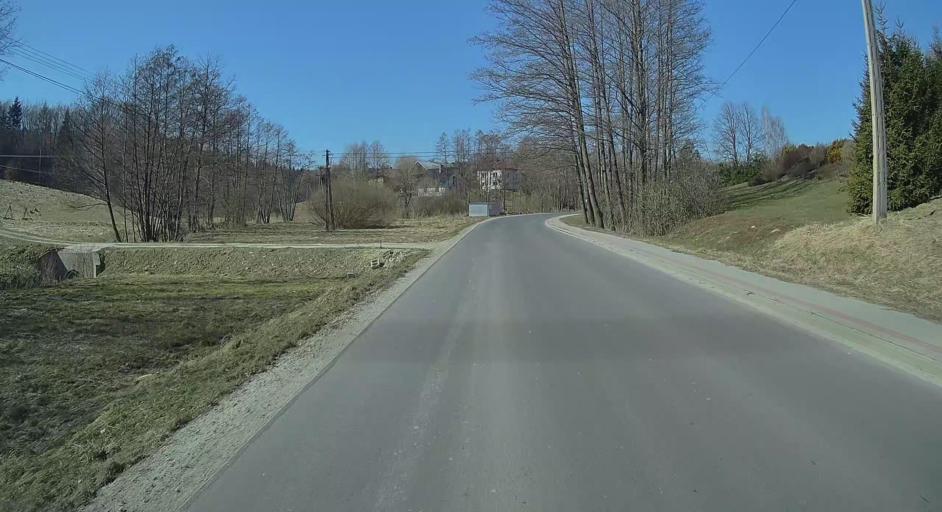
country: PL
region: Subcarpathian Voivodeship
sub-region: Powiat rzeszowski
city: Hyzne
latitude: 49.8875
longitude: 22.2294
